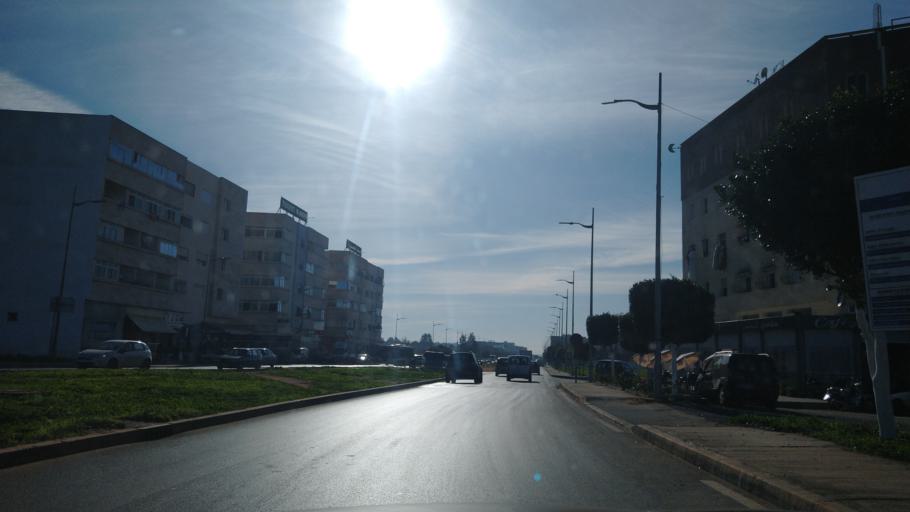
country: MA
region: Rabat-Sale-Zemmour-Zaer
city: Sale
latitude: 34.0128
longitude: -6.7361
